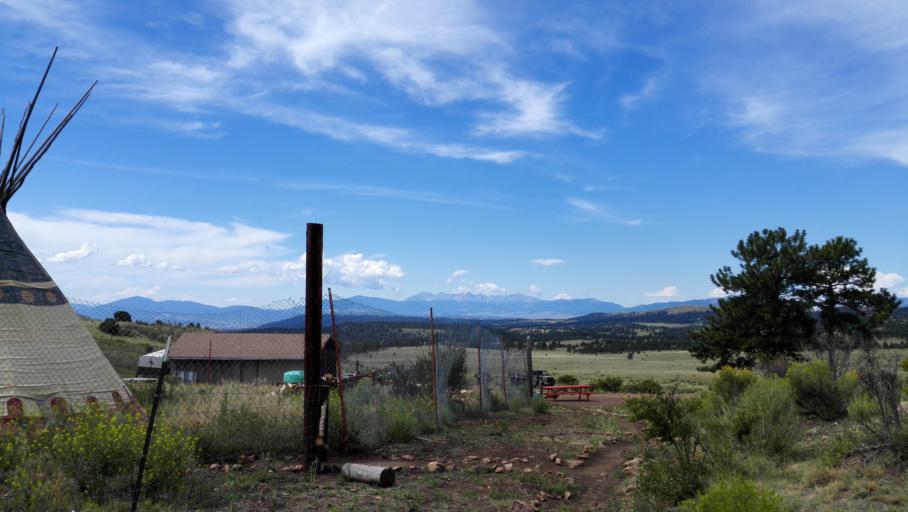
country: US
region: Colorado
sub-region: Custer County
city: Westcliffe
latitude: 37.9607
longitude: -105.2155
